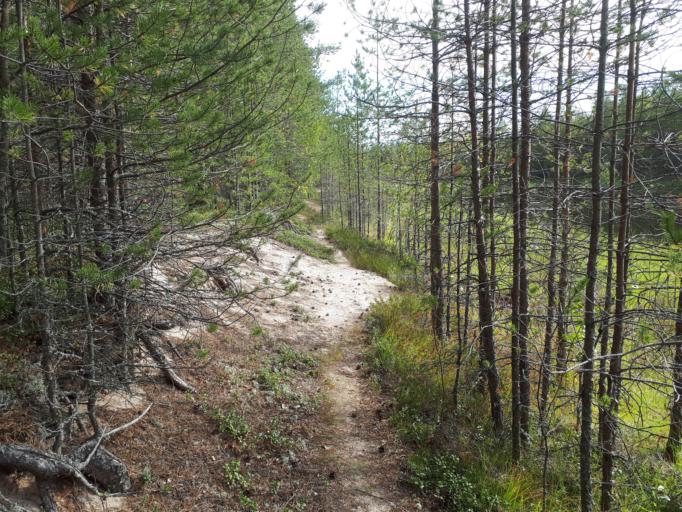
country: FI
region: Northern Ostrobothnia
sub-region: Oulunkaari
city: Ii
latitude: 65.2900
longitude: 25.3808
